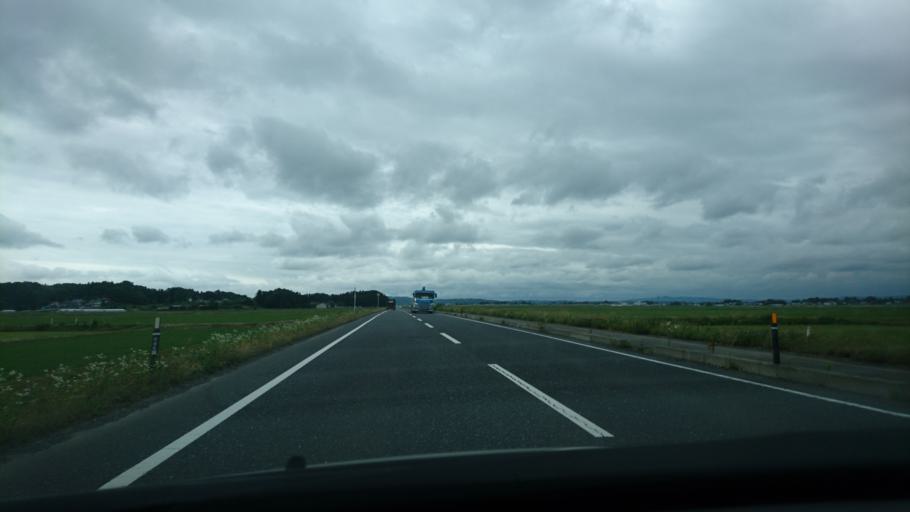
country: JP
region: Miyagi
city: Wakuya
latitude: 38.7040
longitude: 141.2601
